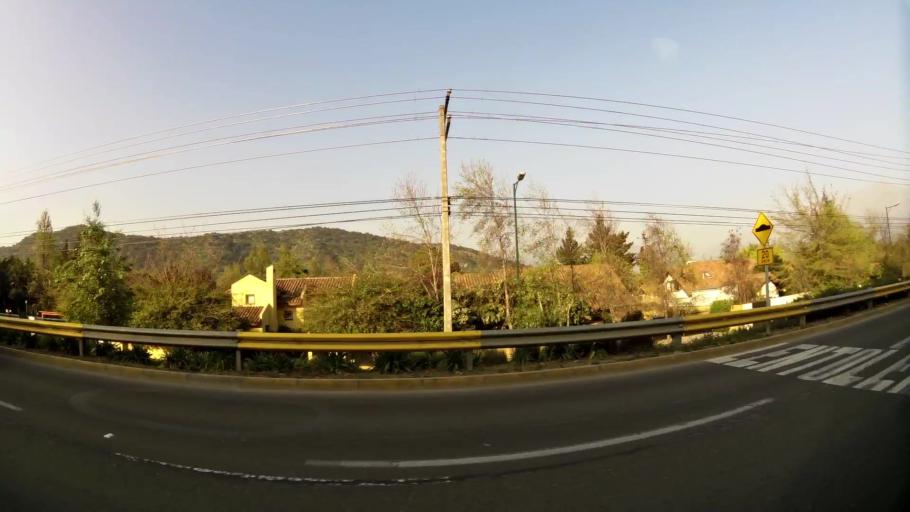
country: CL
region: Santiago Metropolitan
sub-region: Provincia de Santiago
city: Villa Presidente Frei, Nunoa, Santiago, Chile
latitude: -33.3519
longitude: -70.5406
